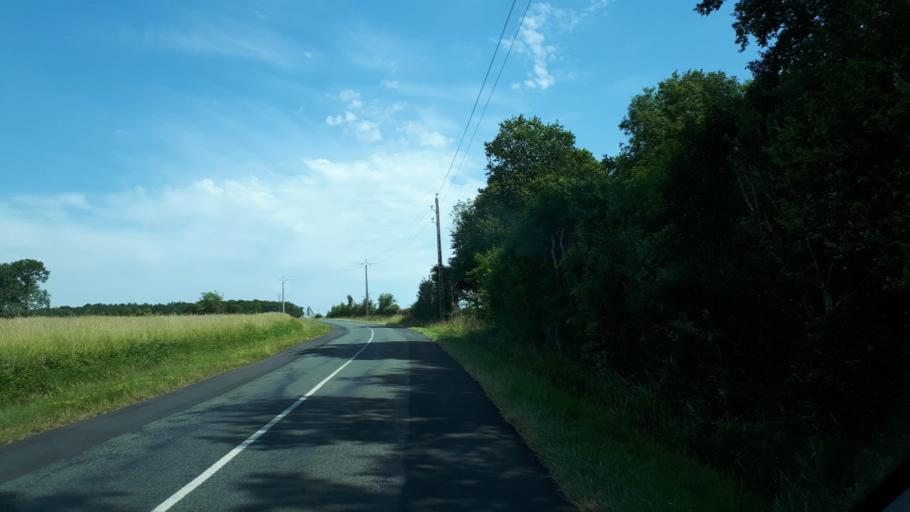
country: FR
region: Centre
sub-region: Departement du Loir-et-Cher
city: Aze
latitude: 47.8622
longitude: 1.0041
